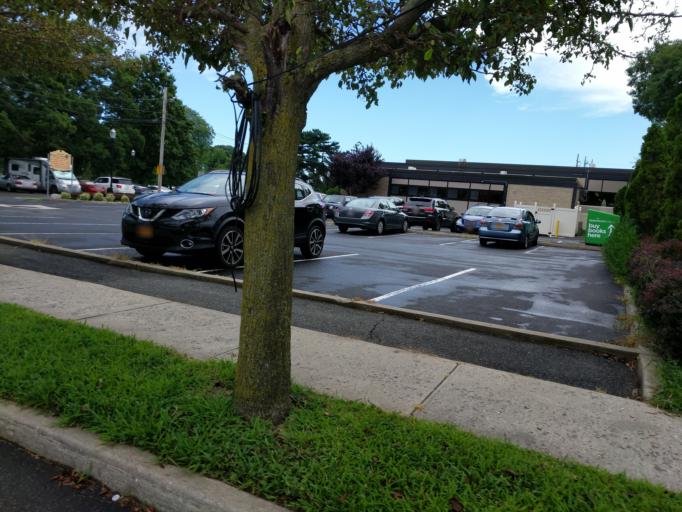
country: US
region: New York
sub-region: Nassau County
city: Valley Stream
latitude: 40.6642
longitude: -73.7072
